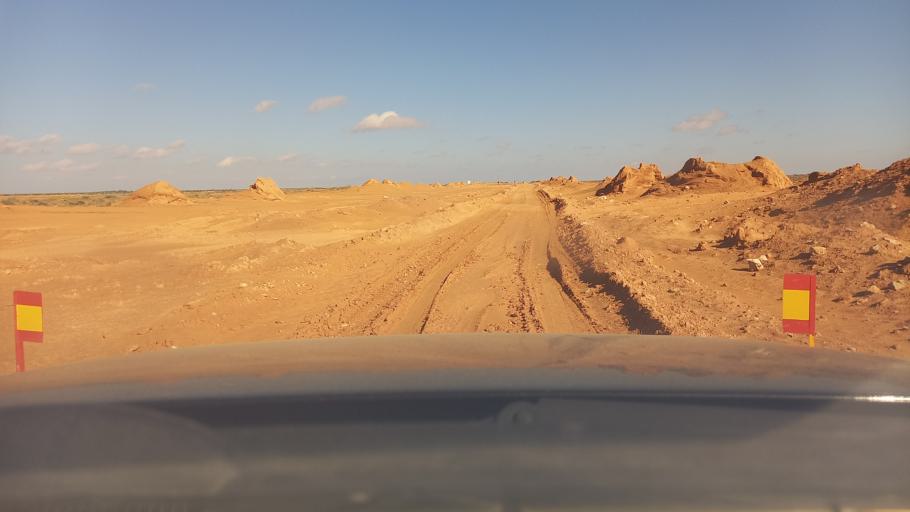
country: TN
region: Madanin
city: Medenine
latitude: 33.2441
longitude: 10.5591
